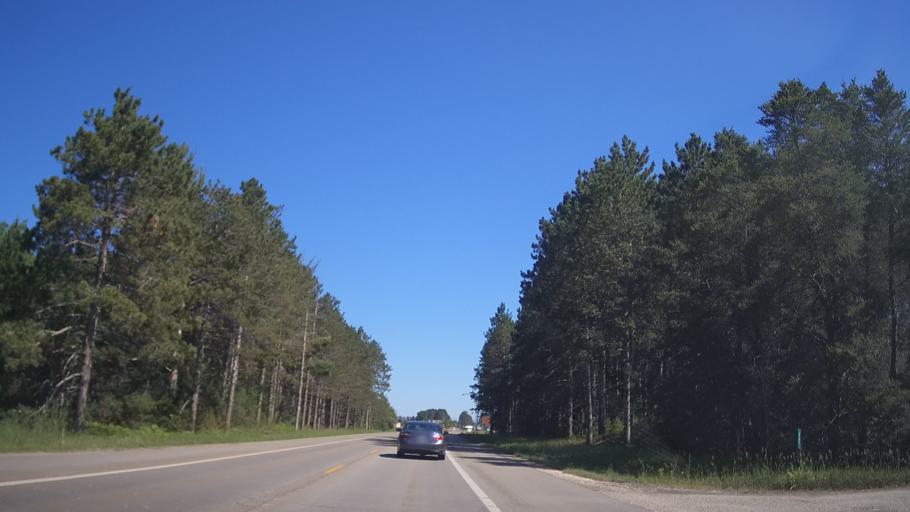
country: US
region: Michigan
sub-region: Cheboygan County
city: Indian River
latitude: 45.5464
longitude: -84.7844
